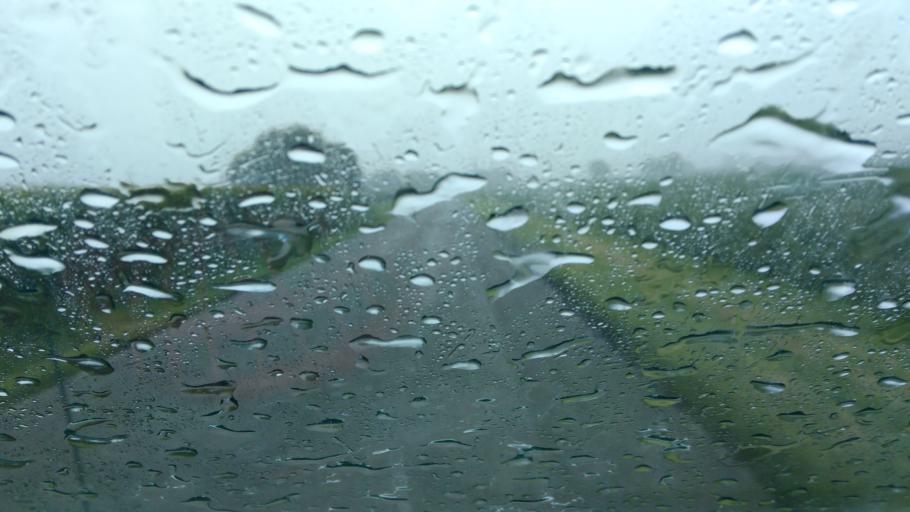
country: US
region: Ohio
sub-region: Hardin County
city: Kenton
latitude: 40.6981
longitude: -83.5379
